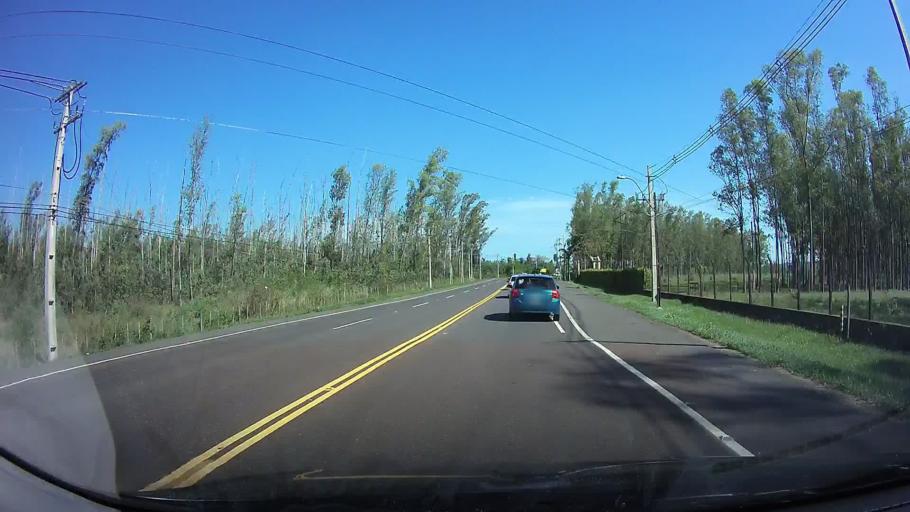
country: PY
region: Central
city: Ypacarai
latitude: -25.3799
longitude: -57.2626
